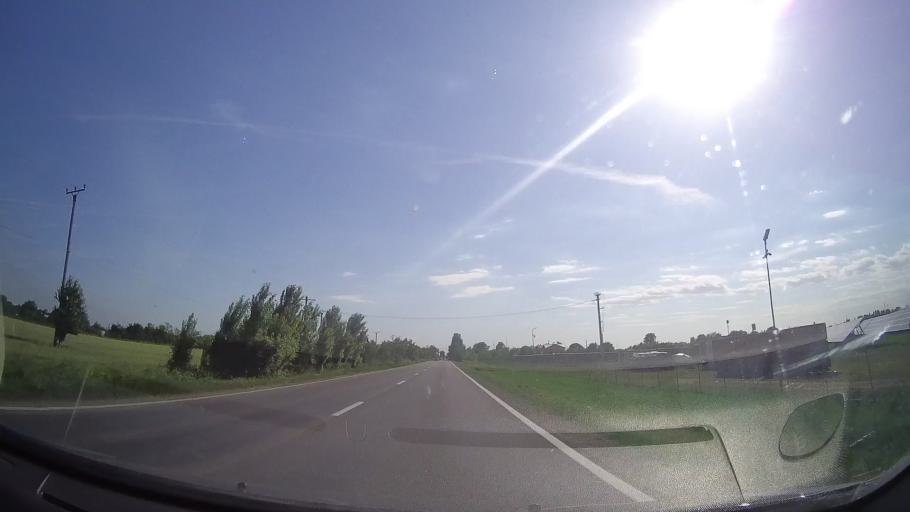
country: RO
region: Prahova
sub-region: Comuna Berceni
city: Corlatesti
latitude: 44.9042
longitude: 26.0707
